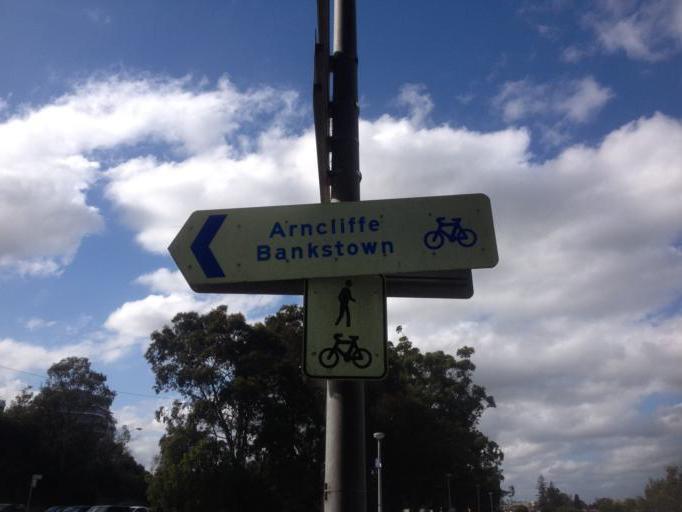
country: AU
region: New South Wales
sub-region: Rockdale
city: Arncliffe
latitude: -33.9306
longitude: 151.1557
